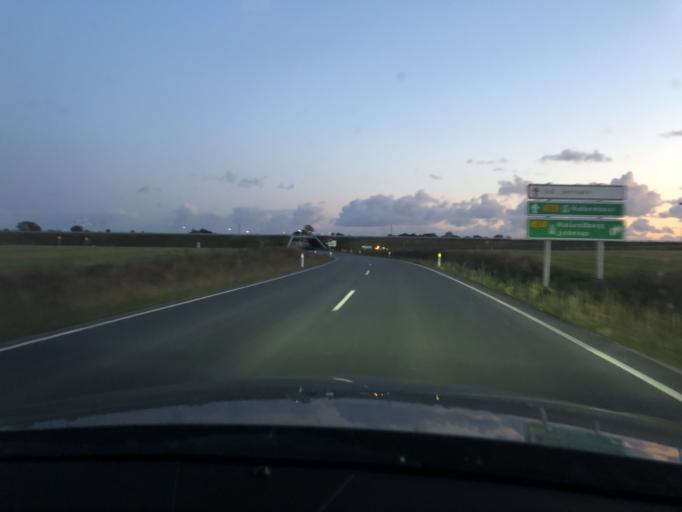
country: DK
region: Zealand
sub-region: Holbaek Kommune
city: Holbaek
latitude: 55.6603
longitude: 11.6324
